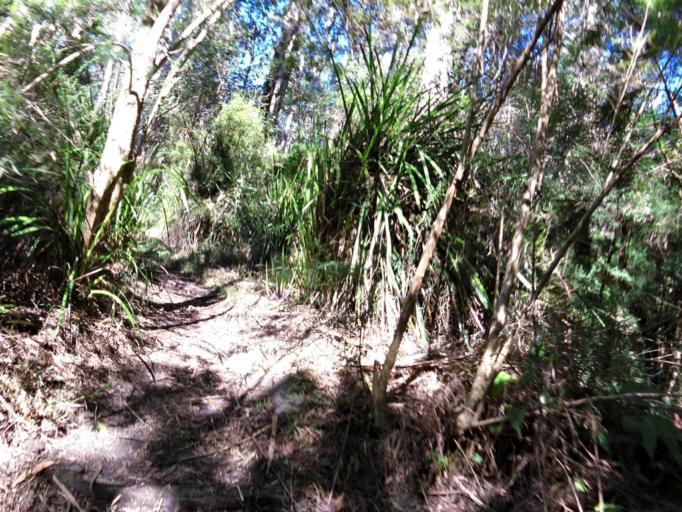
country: AU
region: Victoria
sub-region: Yarra Ranges
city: Millgrove
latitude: -37.7585
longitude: 145.6824
